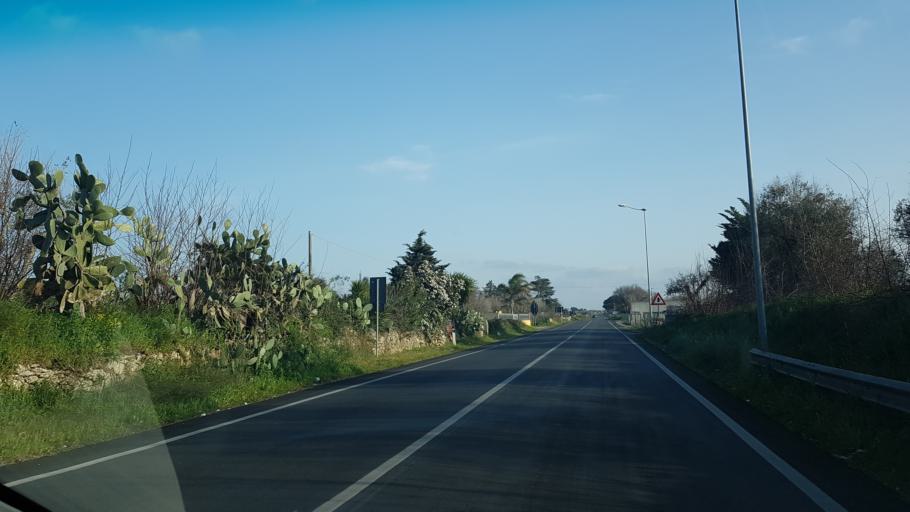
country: IT
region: Apulia
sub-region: Provincia di Lecce
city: Squinzano
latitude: 40.4269
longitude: 18.0536
